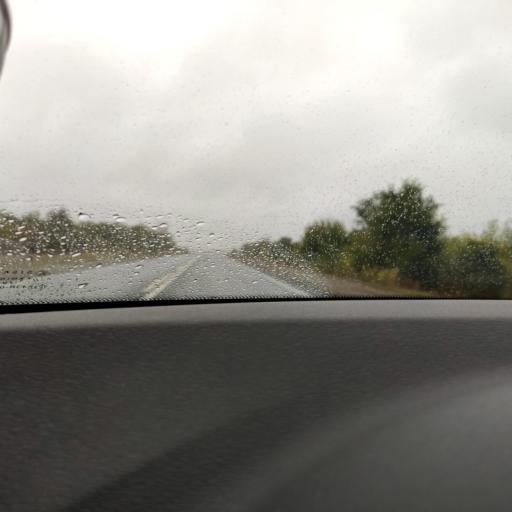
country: RU
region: Samara
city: Mirnyy
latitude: 53.6381
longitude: 50.2327
